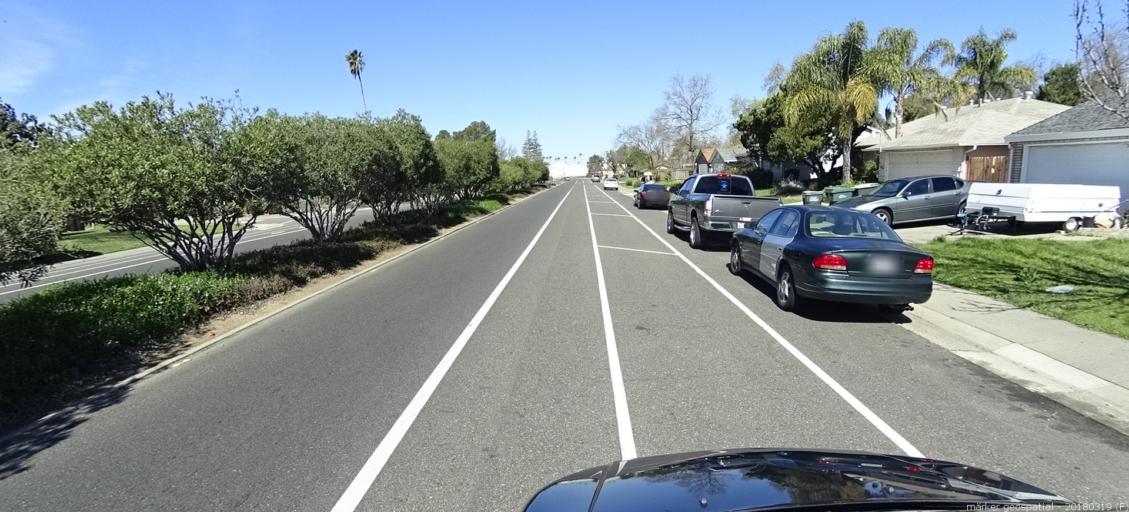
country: US
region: California
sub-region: Sacramento County
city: Parkway
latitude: 38.4916
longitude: -121.4514
